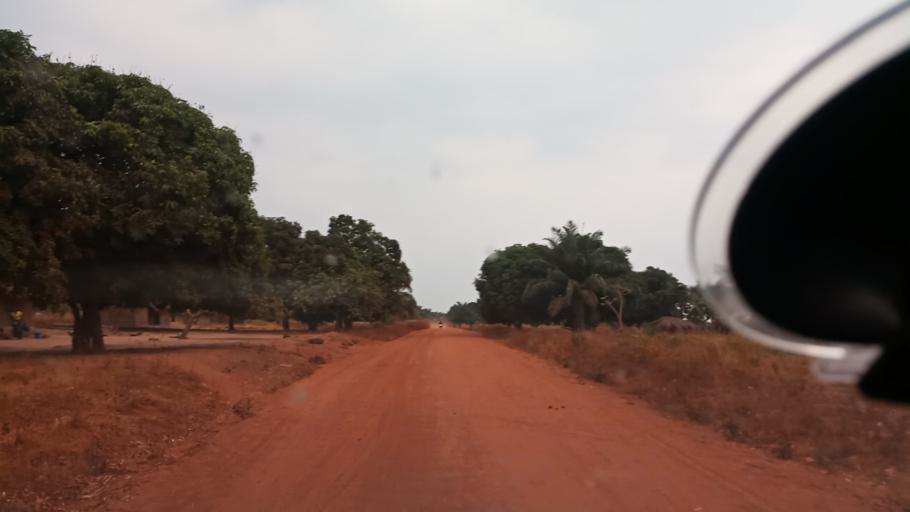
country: ZM
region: Luapula
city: Nchelenge
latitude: -9.1660
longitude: 28.2817
